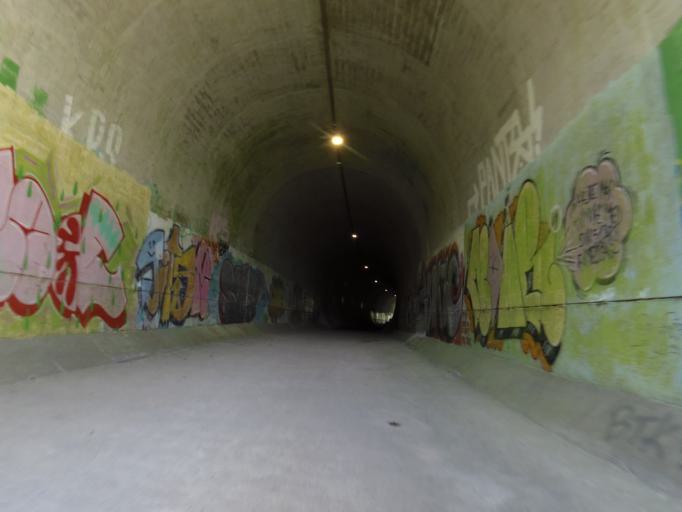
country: DK
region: Central Jutland
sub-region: Skive Kommune
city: Skive
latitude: 56.5685
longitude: 9.0075
